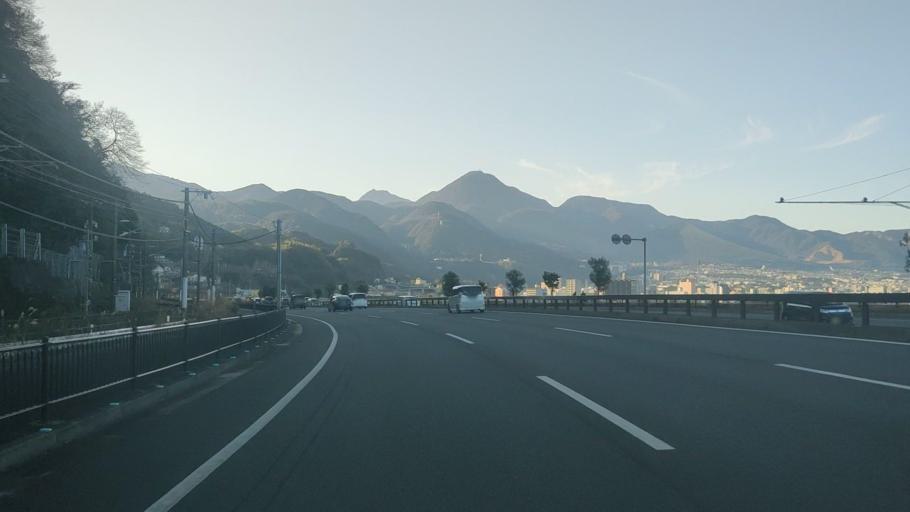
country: JP
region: Oita
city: Beppu
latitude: 33.2651
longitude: 131.5249
